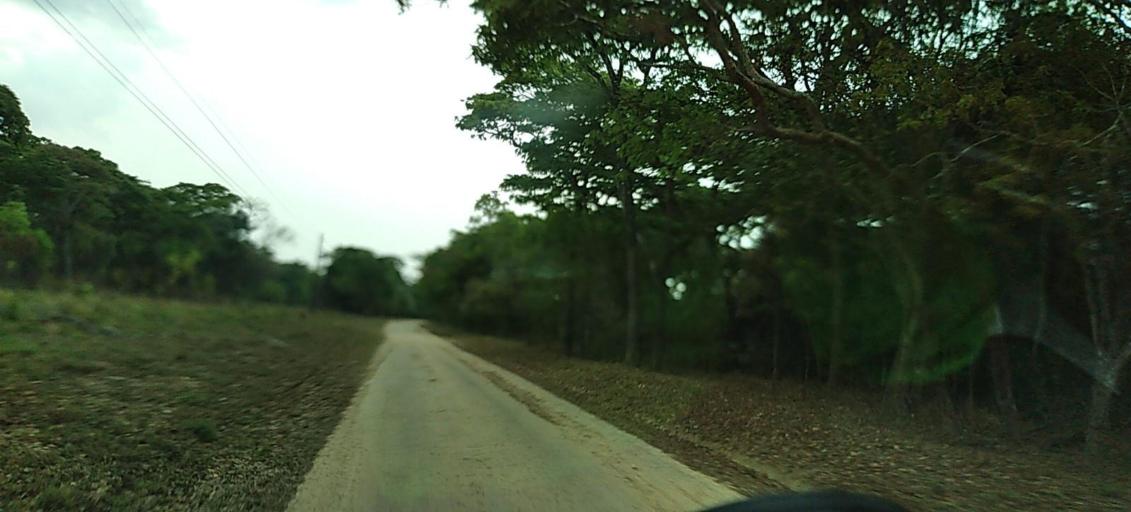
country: ZM
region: North-Western
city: Solwezi
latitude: -12.7668
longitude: 26.4642
